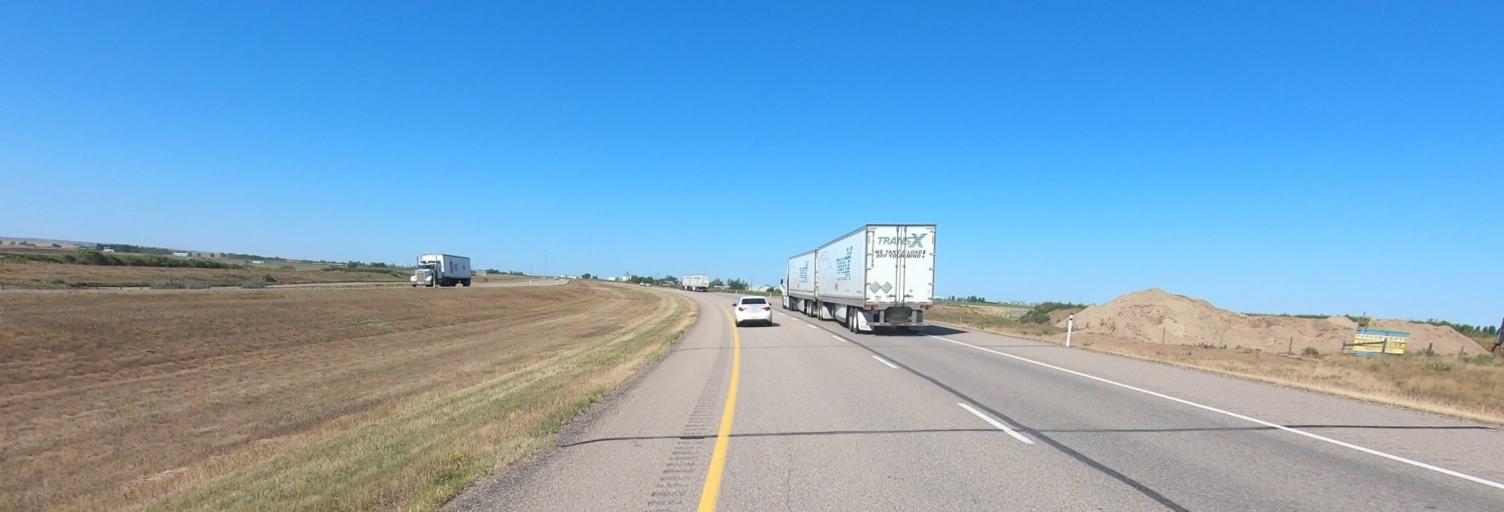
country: CA
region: Alberta
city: Bassano
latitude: 50.7824
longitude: -112.4172
